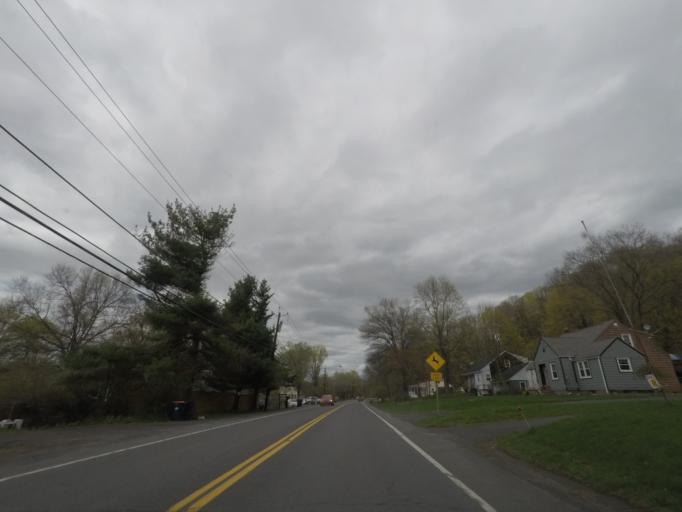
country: US
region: New York
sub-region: Columbia County
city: Chatham
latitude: 42.3374
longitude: -73.6109
